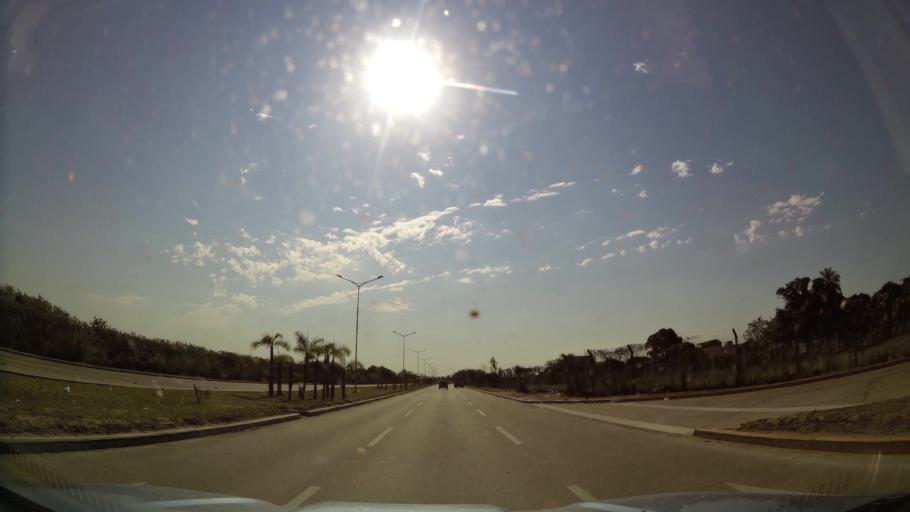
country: BO
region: Santa Cruz
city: Santa Cruz de la Sierra
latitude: -17.8259
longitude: -63.1435
